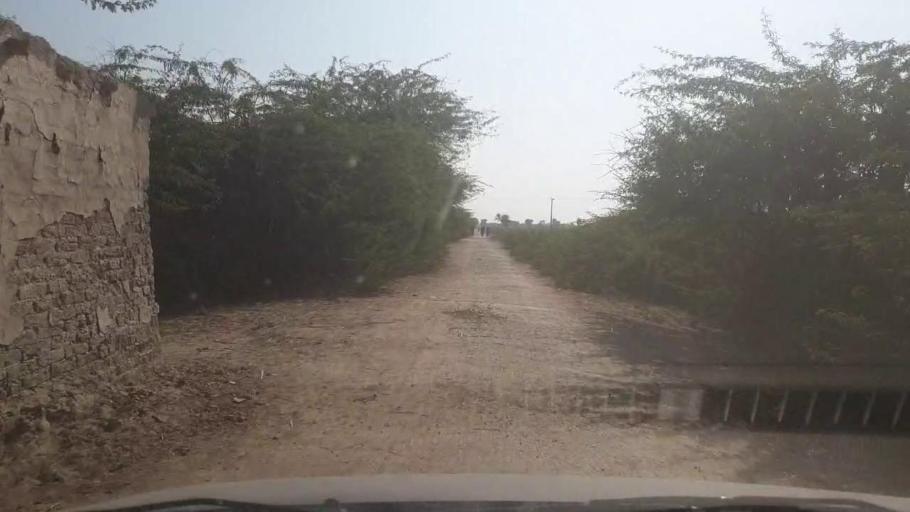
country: PK
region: Sindh
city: Samaro
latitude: 25.1855
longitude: 69.3666
